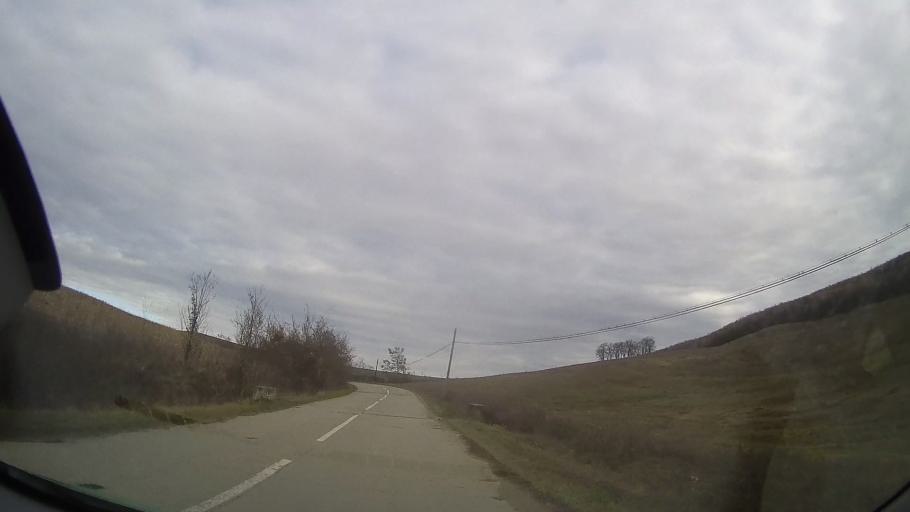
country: RO
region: Bistrita-Nasaud
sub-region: Comuna Micestii de Campie
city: Micestii de Campie
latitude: 46.8475
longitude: 24.3028
